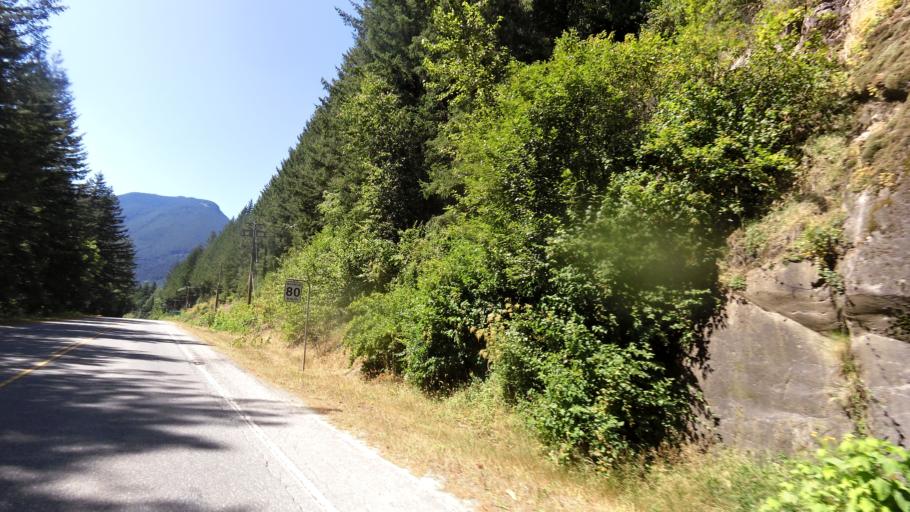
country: CA
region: British Columbia
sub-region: Fraser Valley Regional District
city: Chilliwack
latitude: 49.2447
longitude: -121.9831
